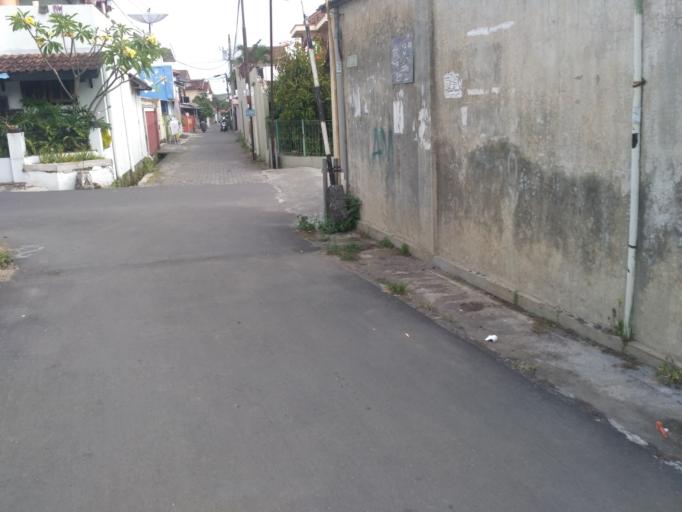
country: ID
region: Daerah Istimewa Yogyakarta
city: Depok
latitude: -7.7763
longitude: 110.4067
